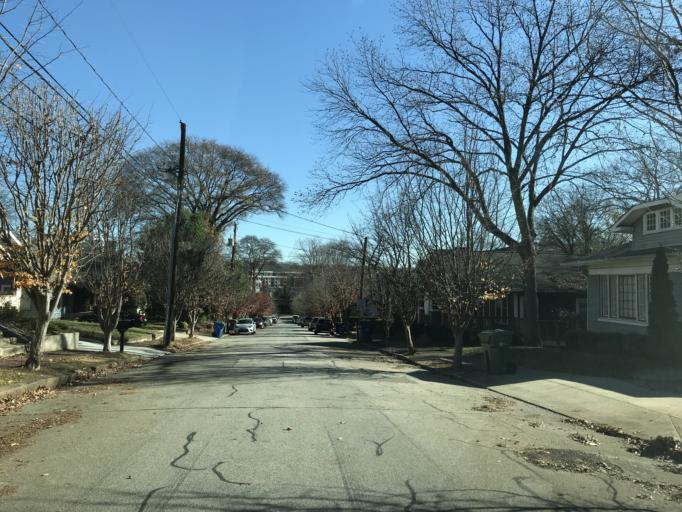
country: US
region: Georgia
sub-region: Fulton County
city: Atlanta
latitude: 33.7699
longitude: -84.3704
